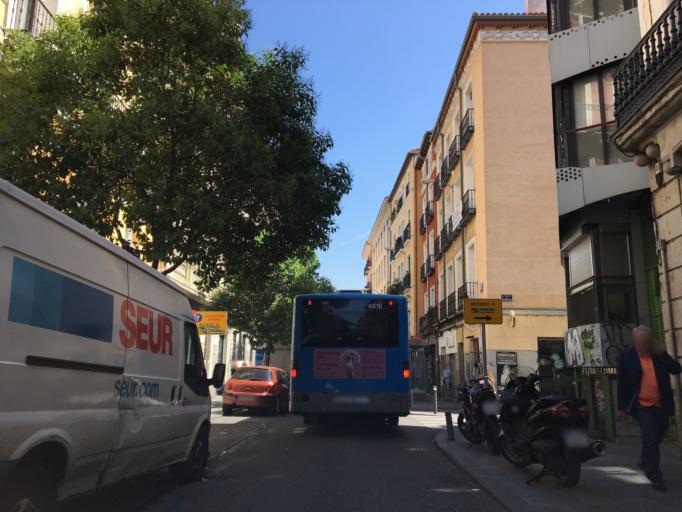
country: ES
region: Madrid
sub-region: Provincia de Madrid
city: City Center
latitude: 40.4232
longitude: -3.6989
